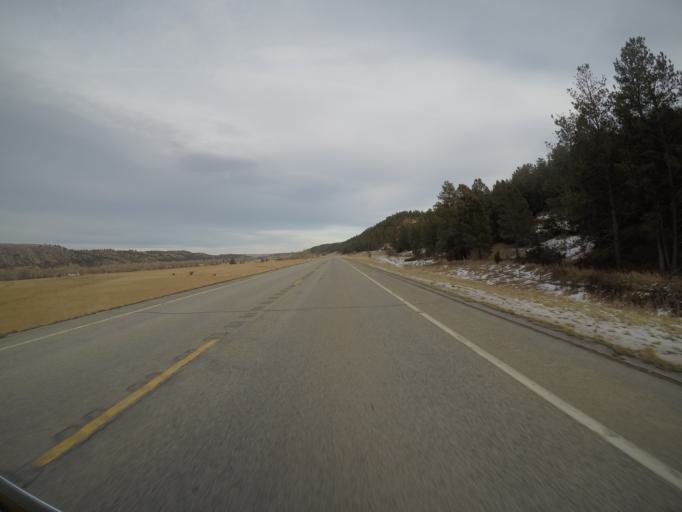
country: US
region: Montana
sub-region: Stillwater County
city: Absarokee
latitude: 45.5542
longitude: -109.3594
